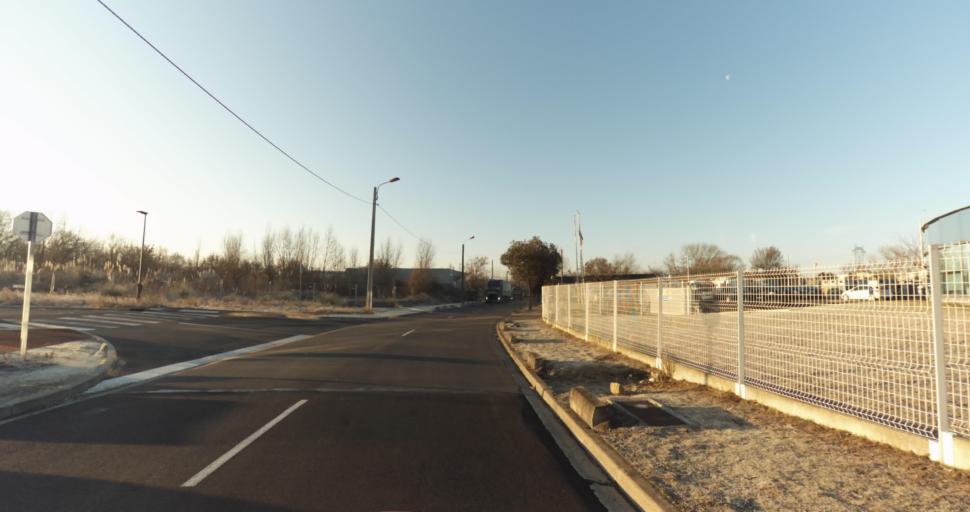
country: FR
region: Aquitaine
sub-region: Departement de la Gironde
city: Ambares-et-Lagrave
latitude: 44.9147
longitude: -0.4866
